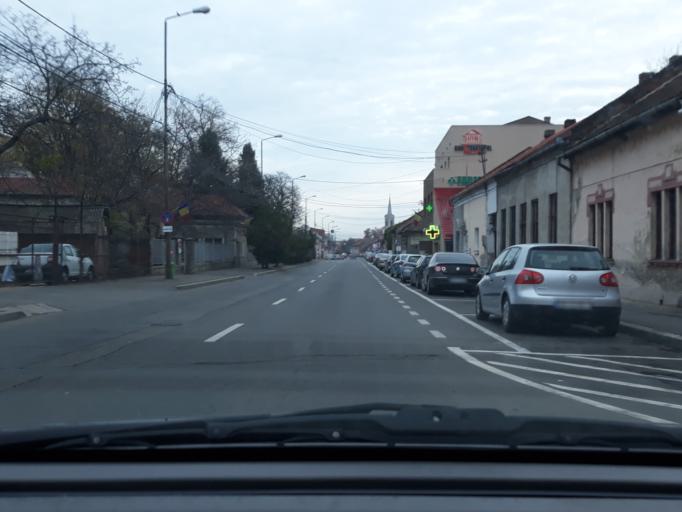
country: RO
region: Bihor
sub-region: Comuna Biharea
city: Oradea
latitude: 47.0528
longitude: 21.9460
